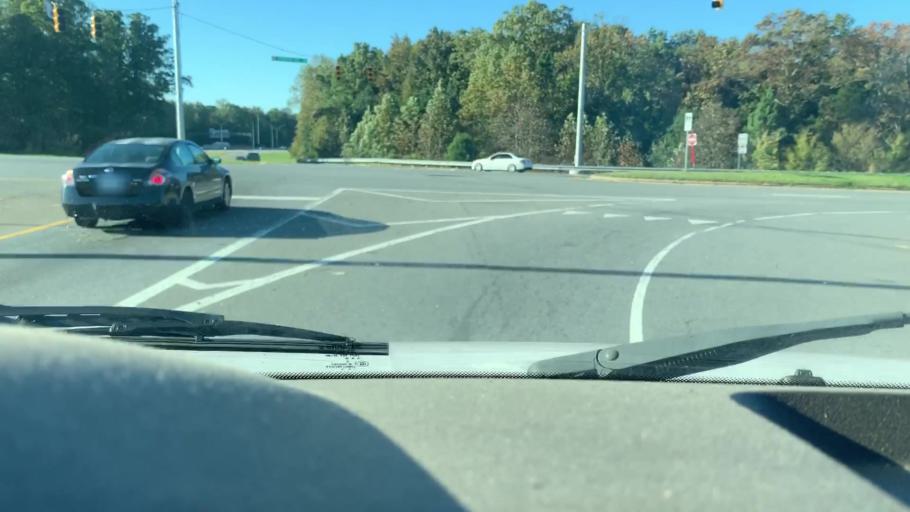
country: US
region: North Carolina
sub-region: Mecklenburg County
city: Charlotte
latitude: 35.2919
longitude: -80.7706
